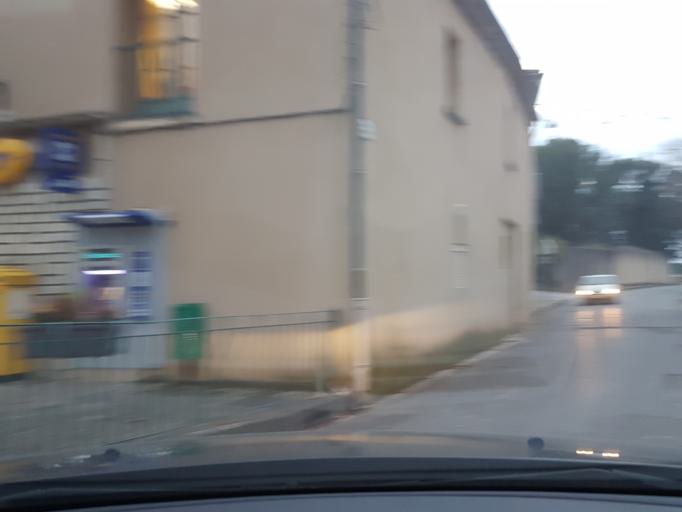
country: FR
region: Provence-Alpes-Cote d'Azur
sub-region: Departement du Vaucluse
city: Loriol-du-Comtat
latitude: 44.0764
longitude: 5.0004
